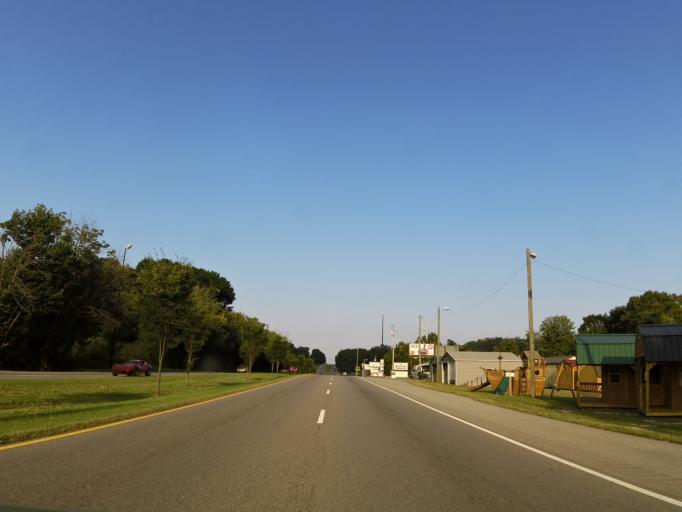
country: US
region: Tennessee
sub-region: Knox County
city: Mascot
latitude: 36.0170
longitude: -83.8232
